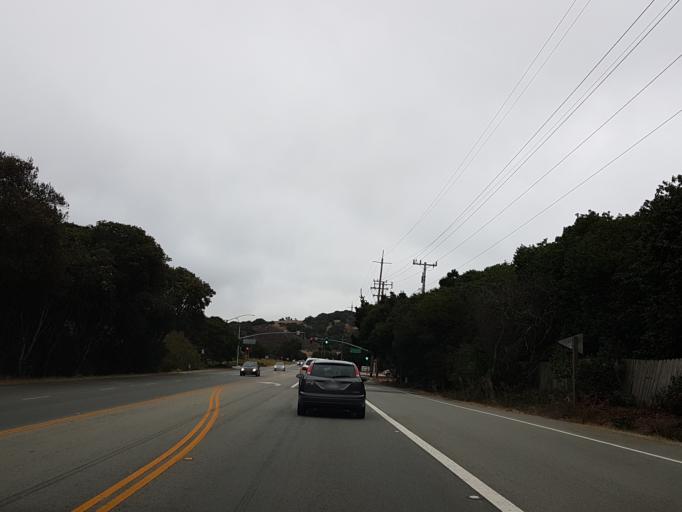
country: US
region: California
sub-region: Monterey County
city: Del Rey Oaks
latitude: 36.5674
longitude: -121.7803
